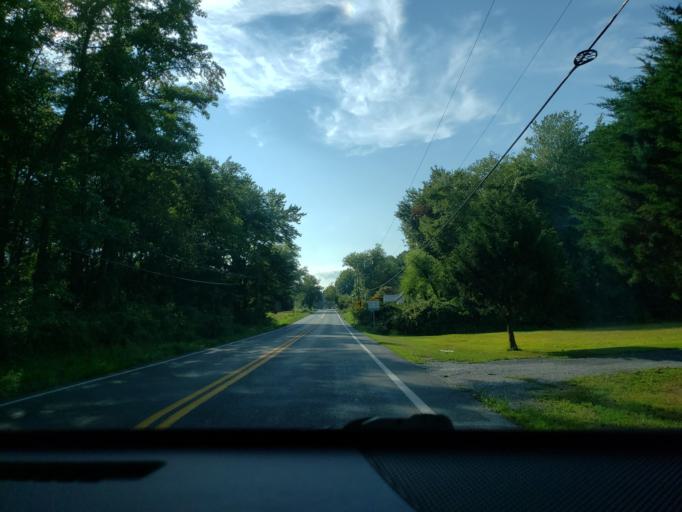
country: US
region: Delaware
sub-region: Sussex County
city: Milton
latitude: 38.7703
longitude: -75.2958
